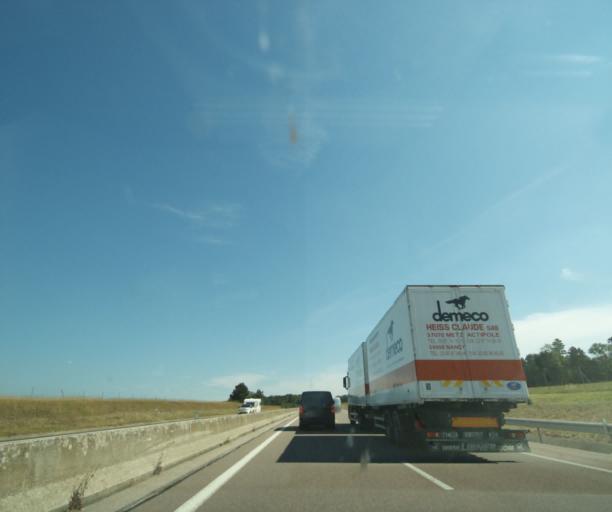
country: FR
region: Lorraine
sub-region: Departement de Meurthe-et-Moselle
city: Colombey-les-Belles
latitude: 48.4355
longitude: 5.8616
